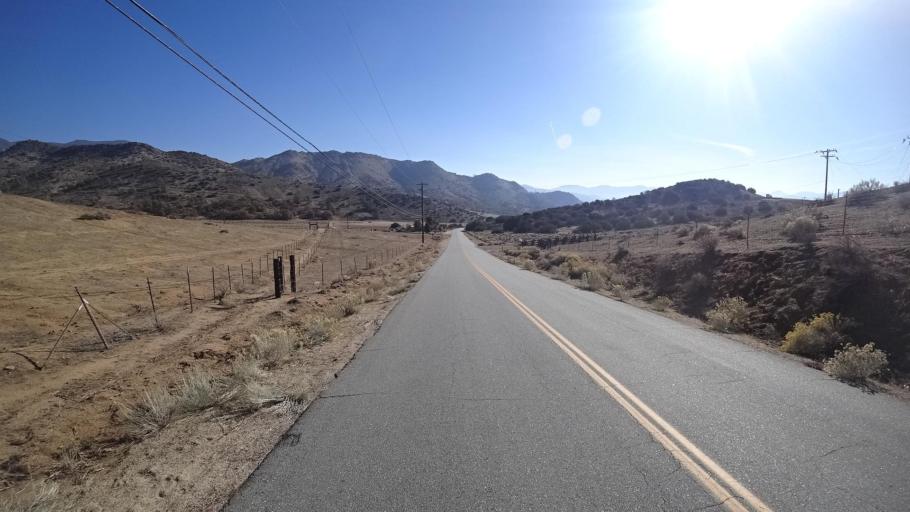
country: US
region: California
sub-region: Kern County
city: Bodfish
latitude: 35.3681
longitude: -118.3894
